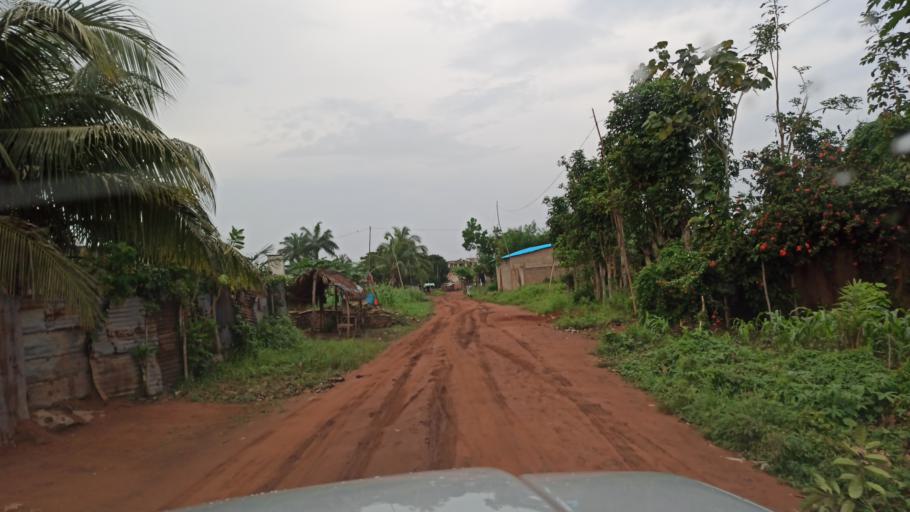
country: BJ
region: Queme
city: Porto-Novo
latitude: 6.4741
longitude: 2.6739
